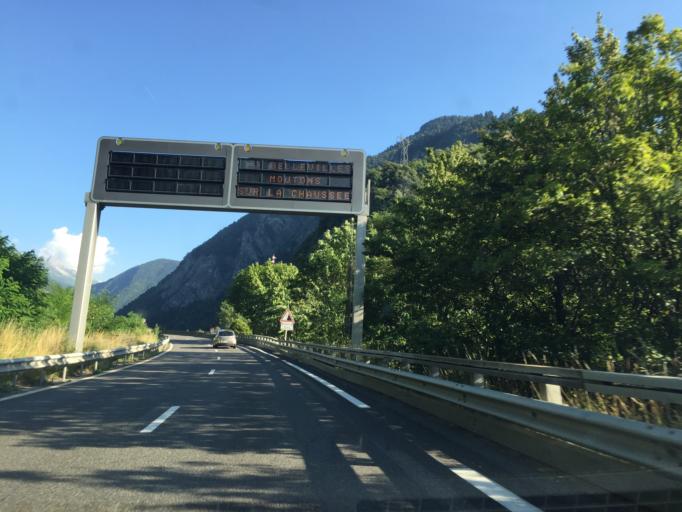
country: FR
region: Rhone-Alpes
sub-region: Departement de la Savoie
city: Aigueblanche
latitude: 45.4985
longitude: 6.5127
